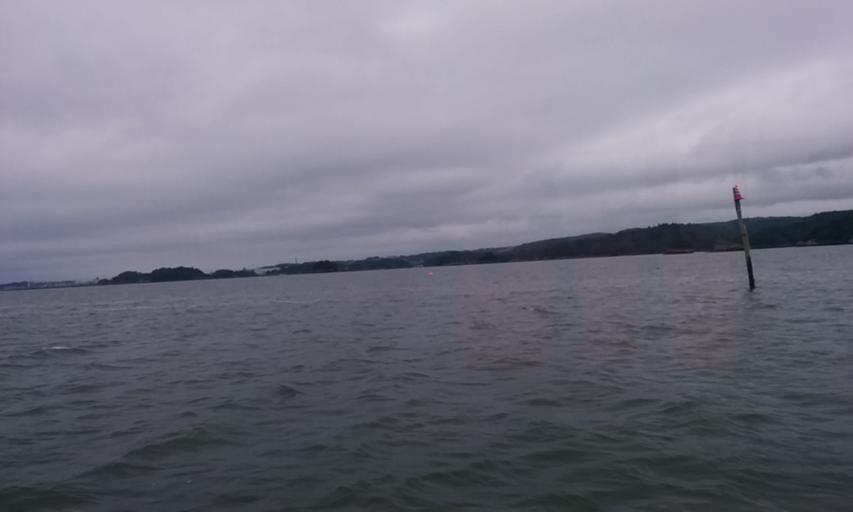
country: JP
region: Miyagi
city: Matsushima
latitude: 38.3502
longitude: 141.0747
